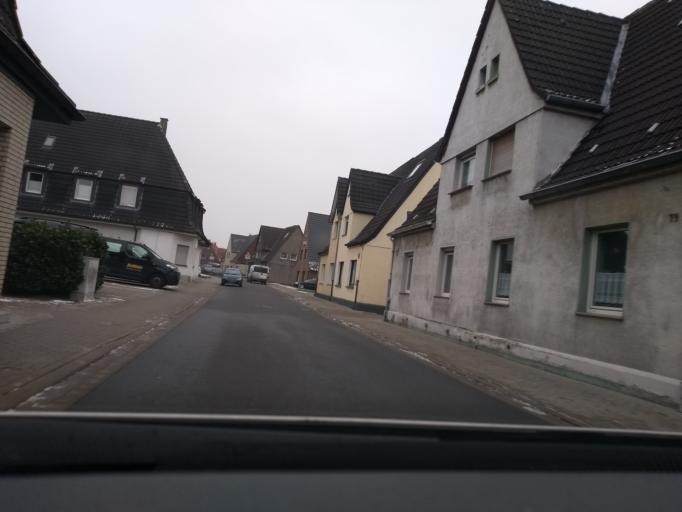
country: DE
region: North Rhine-Westphalia
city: Selm
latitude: 51.6942
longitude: 7.4614
